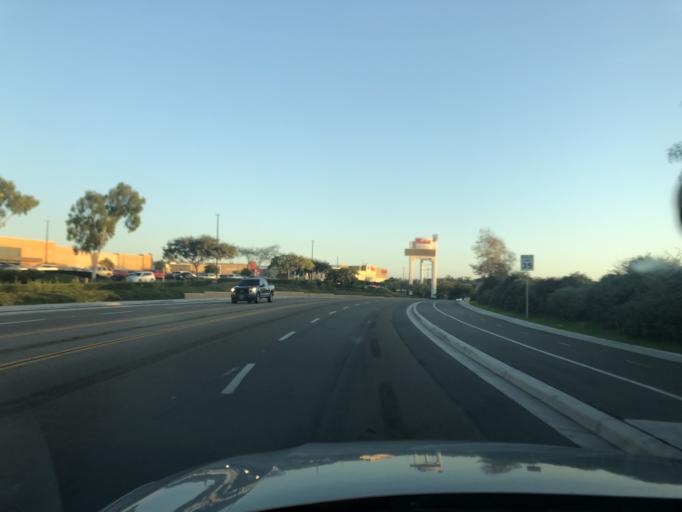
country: US
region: California
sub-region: San Diego County
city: Chula Vista
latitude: 32.6564
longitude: -117.0684
